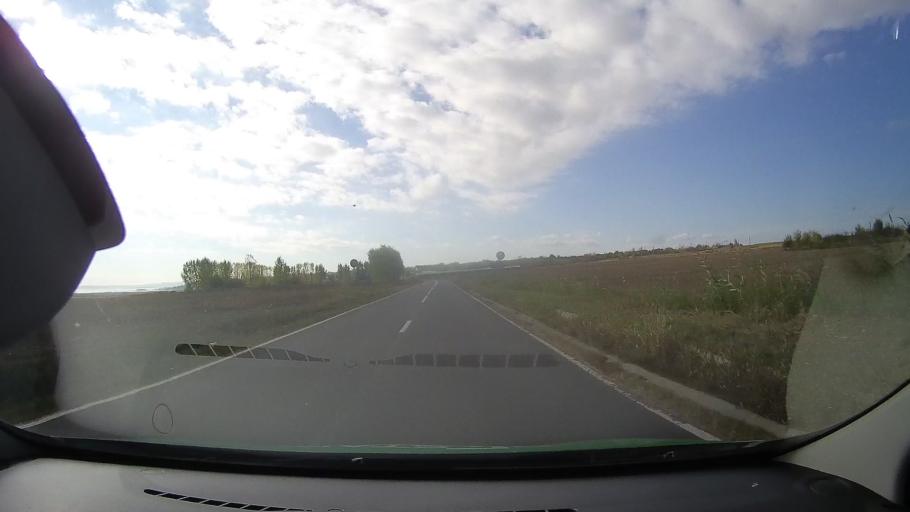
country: RO
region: Tulcea
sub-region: Comuna Sarichioi
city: Sarichioi
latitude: 44.9603
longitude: 28.8592
